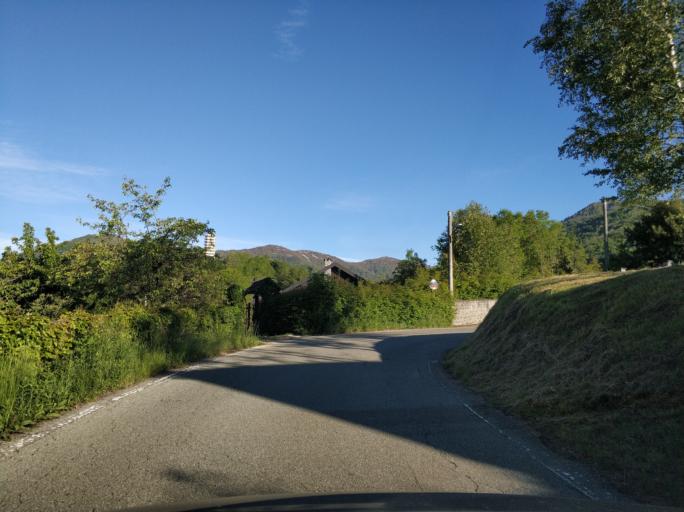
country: IT
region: Piedmont
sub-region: Provincia di Torino
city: Coassolo
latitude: 45.2995
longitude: 7.4662
